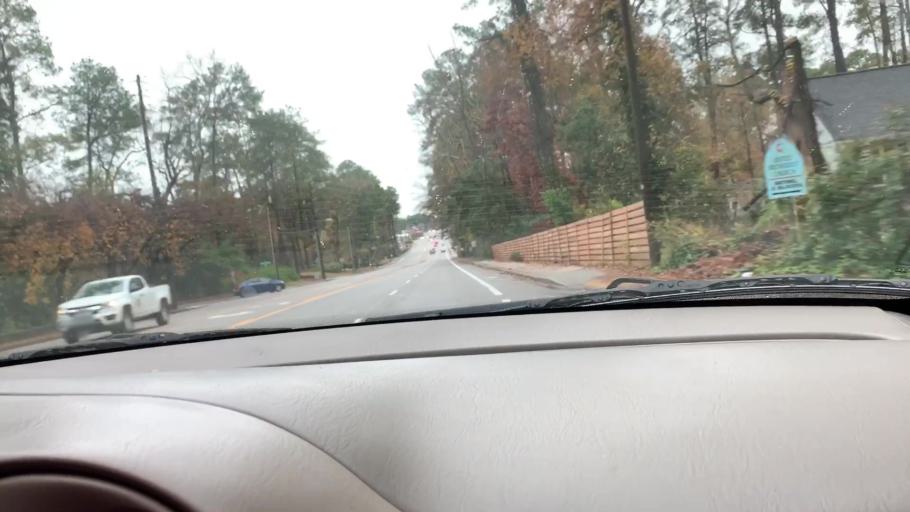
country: US
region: South Carolina
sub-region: Richland County
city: Forest Acres
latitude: 34.0236
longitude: -80.9664
